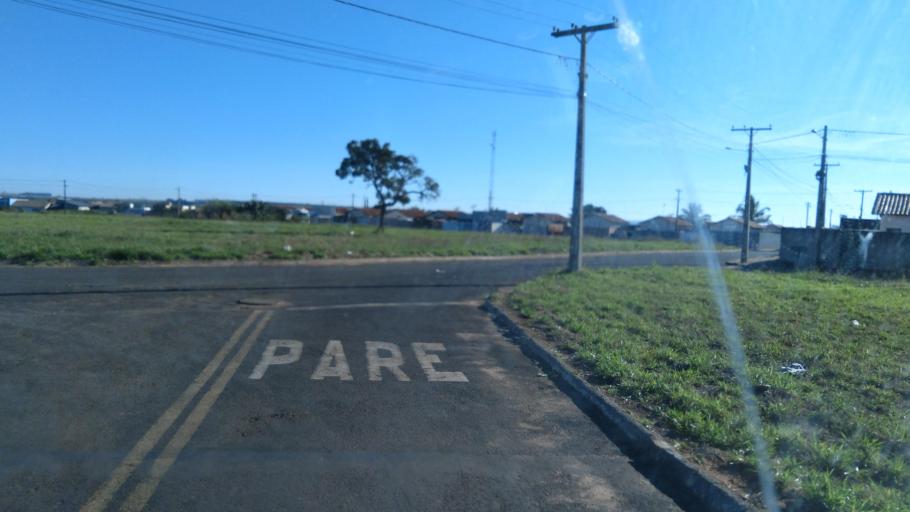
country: BR
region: Goias
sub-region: Mineiros
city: Mineiros
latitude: -17.5448
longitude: -52.5504
